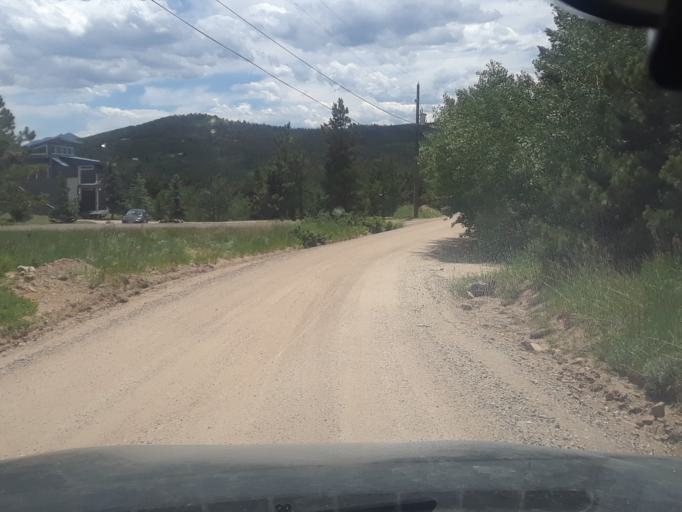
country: US
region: Colorado
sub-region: Boulder County
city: Nederland
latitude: 39.9681
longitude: -105.5096
